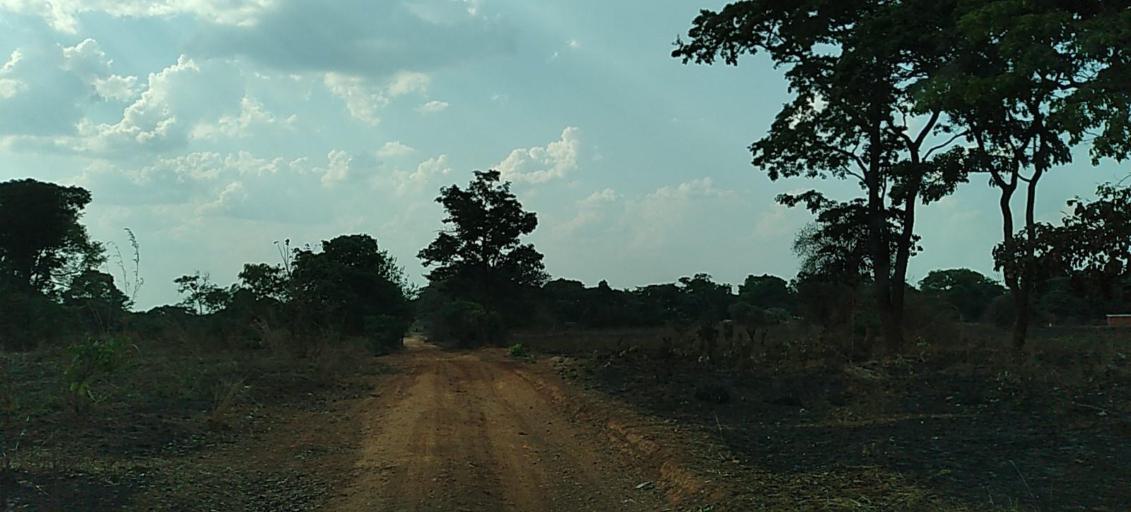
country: ZM
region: Copperbelt
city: Mpongwe
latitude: -13.5142
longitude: 28.0987
